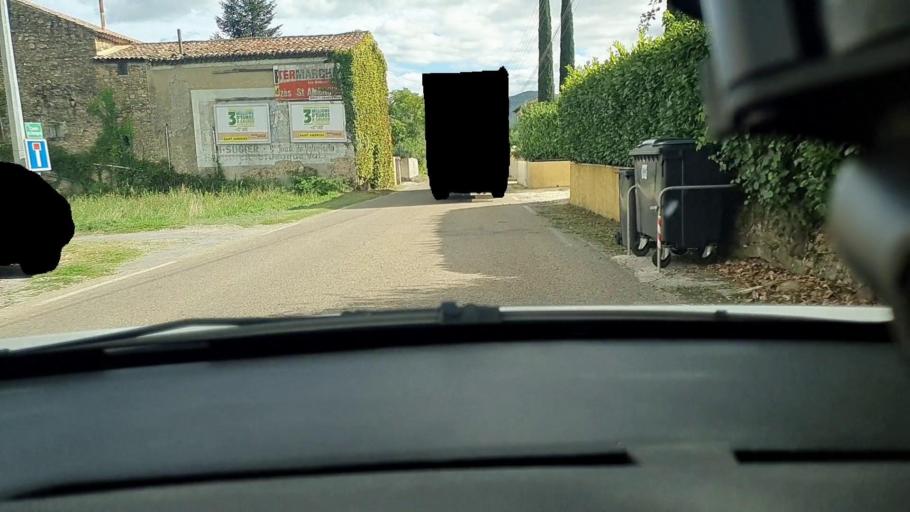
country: FR
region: Languedoc-Roussillon
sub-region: Departement du Gard
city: Saint-Florent-sur-Auzonnet
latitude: 44.2453
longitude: 4.0992
